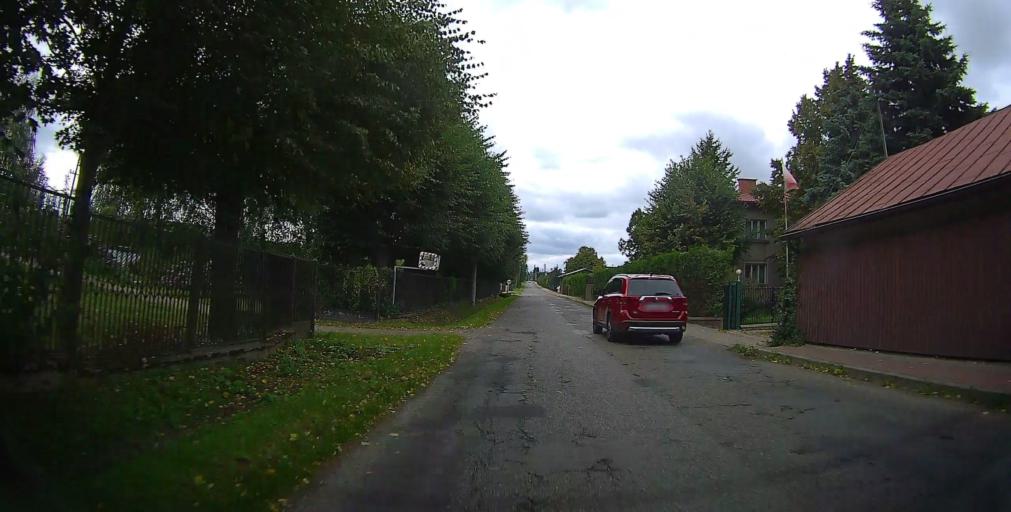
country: PL
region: Masovian Voivodeship
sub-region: Powiat grojecki
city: Belsk Duzy
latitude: 51.8211
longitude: 20.8182
